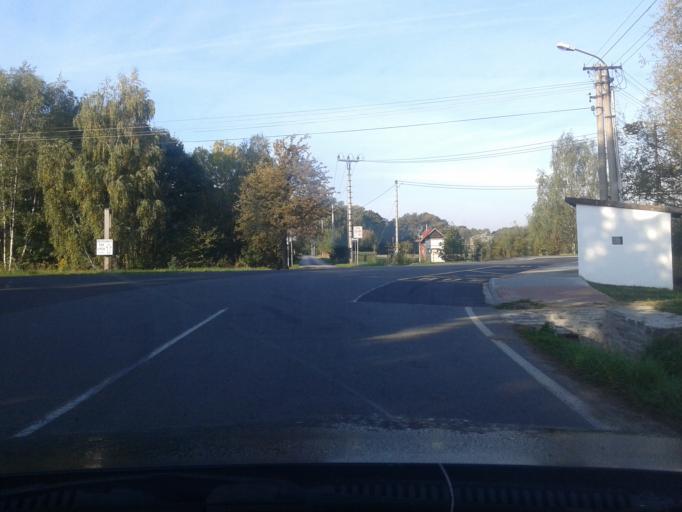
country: CZ
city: Rychvald
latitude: 49.8831
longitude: 18.3837
